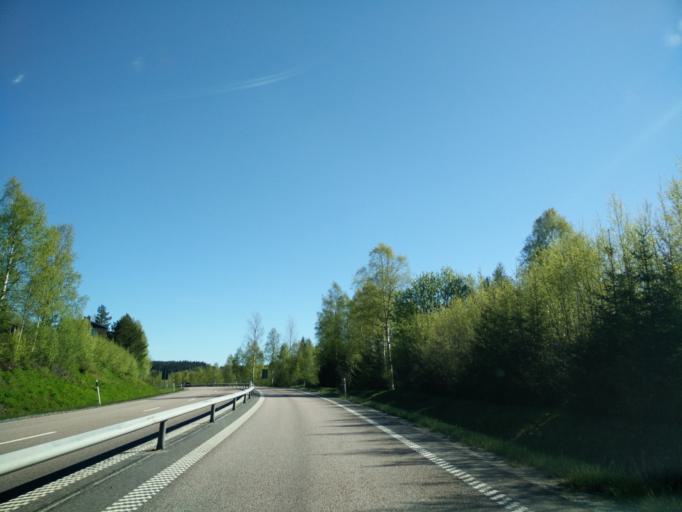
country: SE
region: Vaesternorrland
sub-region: OErnskoeldsviks Kommun
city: Bjasta
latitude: 63.1701
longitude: 18.4320
